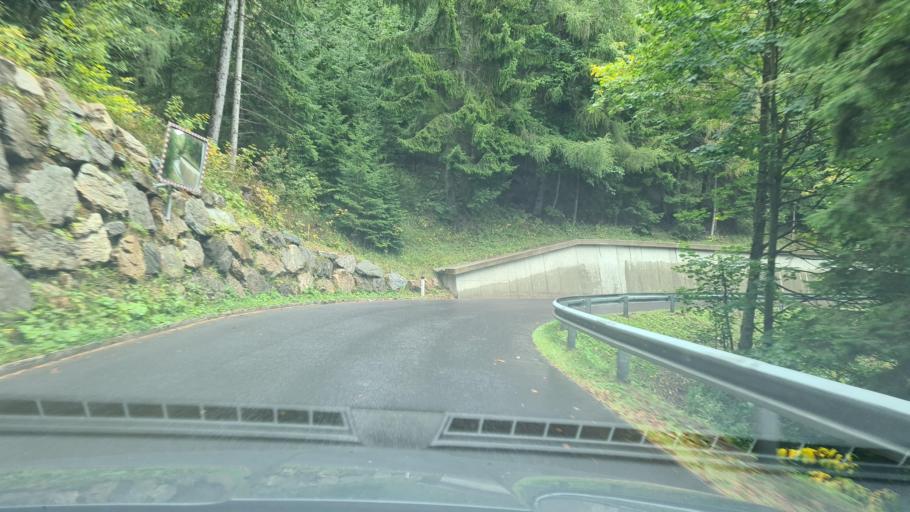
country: AT
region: Styria
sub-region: Politischer Bezirk Weiz
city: Passail
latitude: 47.3317
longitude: 15.4744
